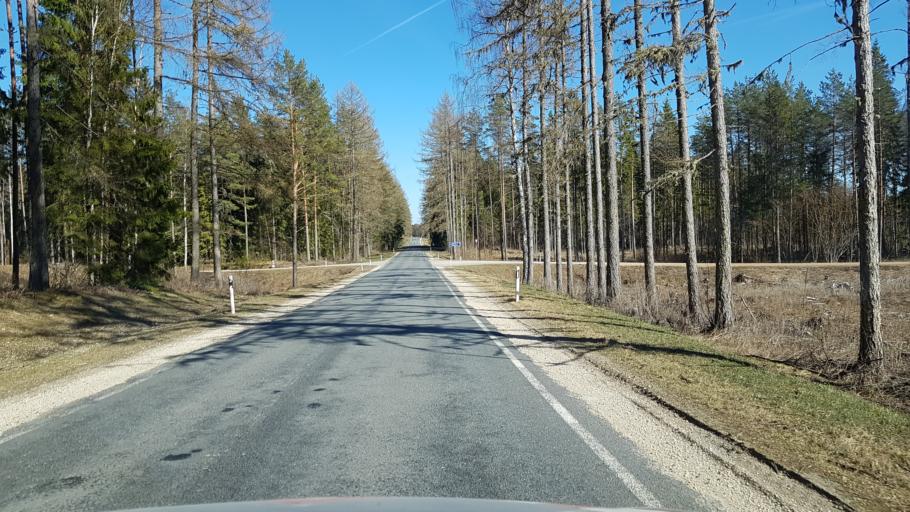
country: EE
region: Laeaene-Virumaa
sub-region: Vinni vald
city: Vinni
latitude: 59.2734
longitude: 26.6291
